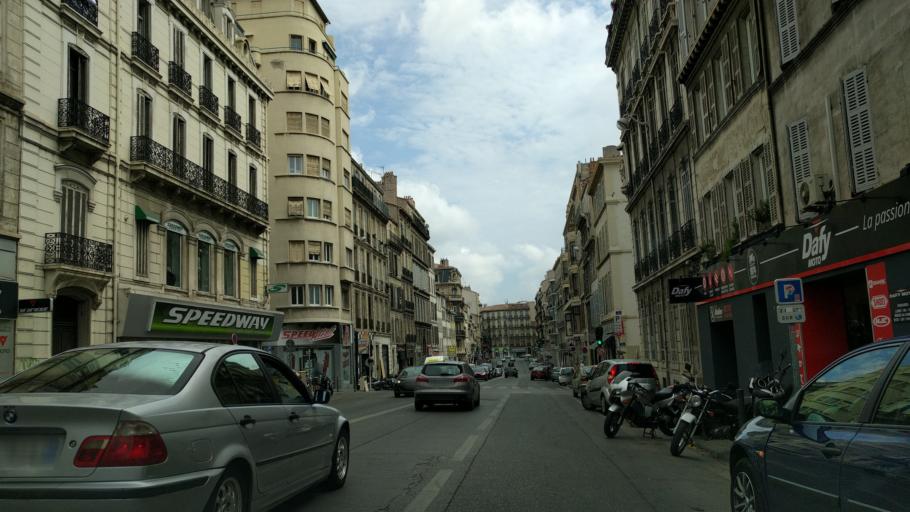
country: FR
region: Provence-Alpes-Cote d'Azur
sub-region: Departement des Bouches-du-Rhone
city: Marseille 06
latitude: 43.2887
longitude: 5.3843
